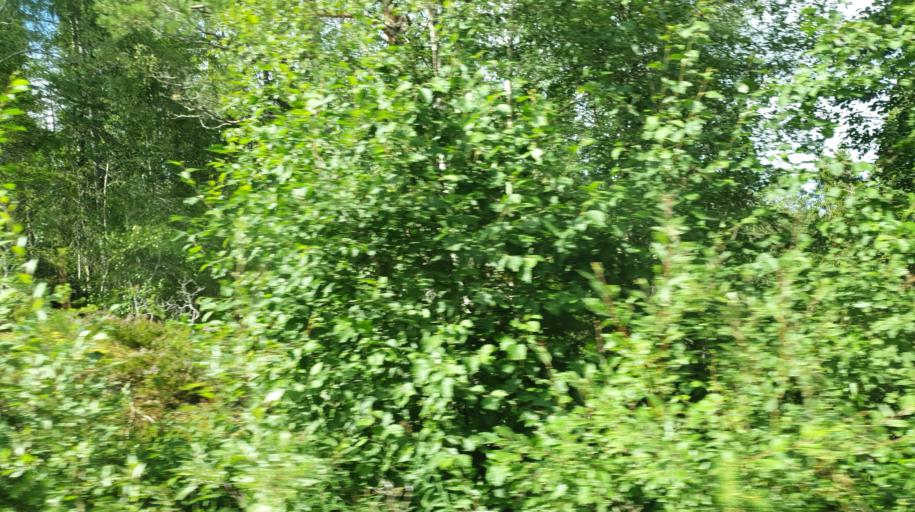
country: NO
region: Nord-Trondelag
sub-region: Levanger
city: Skogn
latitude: 63.5909
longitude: 11.2558
